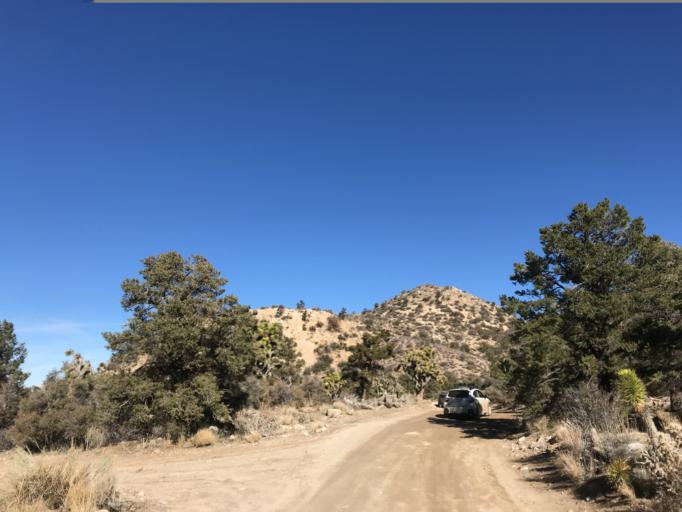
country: US
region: California
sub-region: San Bernardino County
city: Big Bear City
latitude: 34.2309
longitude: -116.6617
